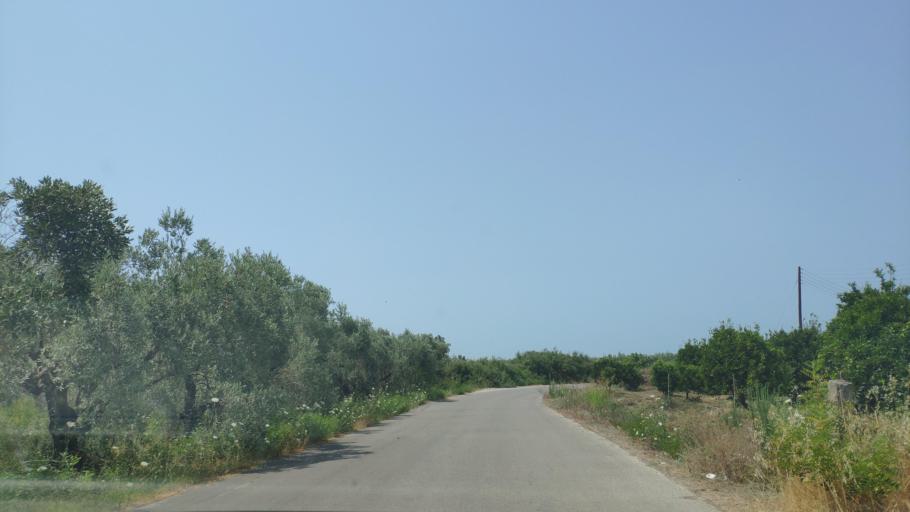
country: GR
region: Epirus
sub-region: Nomos Artas
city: Neochori
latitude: 39.0601
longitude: 21.0480
